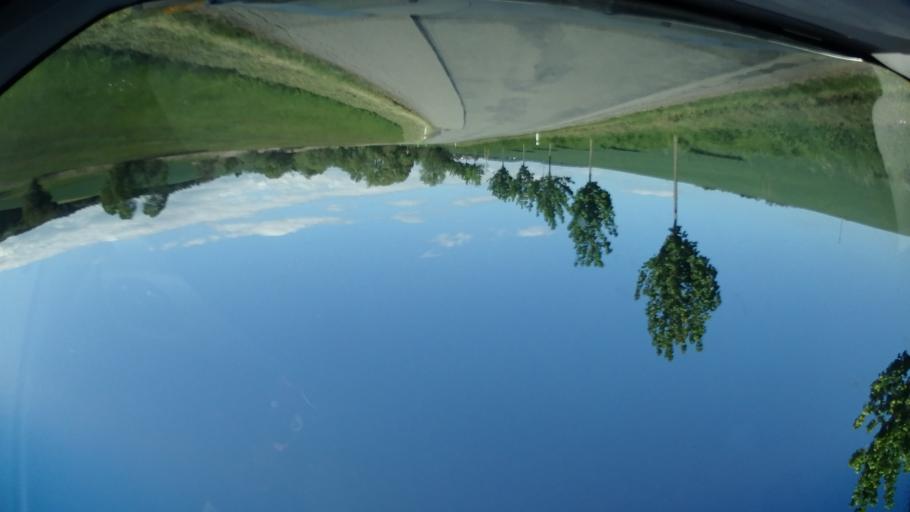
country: CZ
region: South Moravian
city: Velke Opatovice
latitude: 49.6668
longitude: 16.6328
